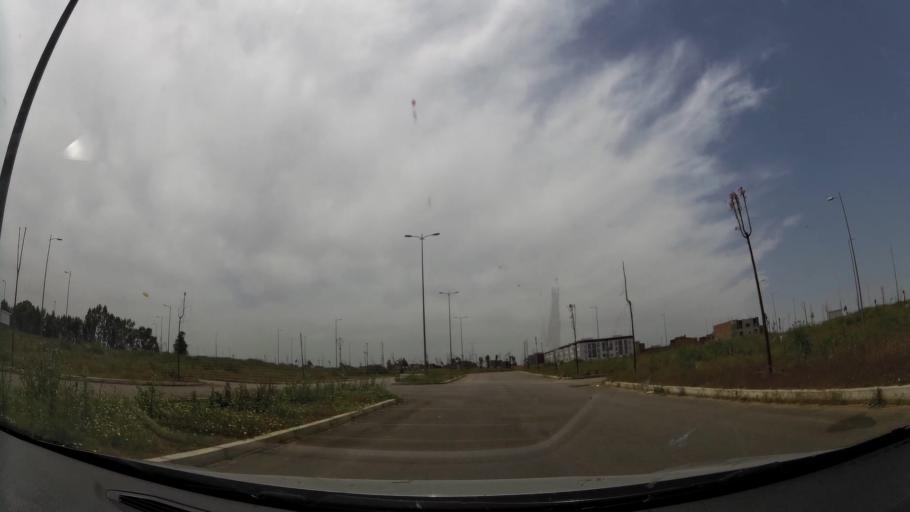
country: MA
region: Rabat-Sale-Zemmour-Zaer
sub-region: Khemisset
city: Khemisset
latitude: 33.8165
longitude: -6.0861
